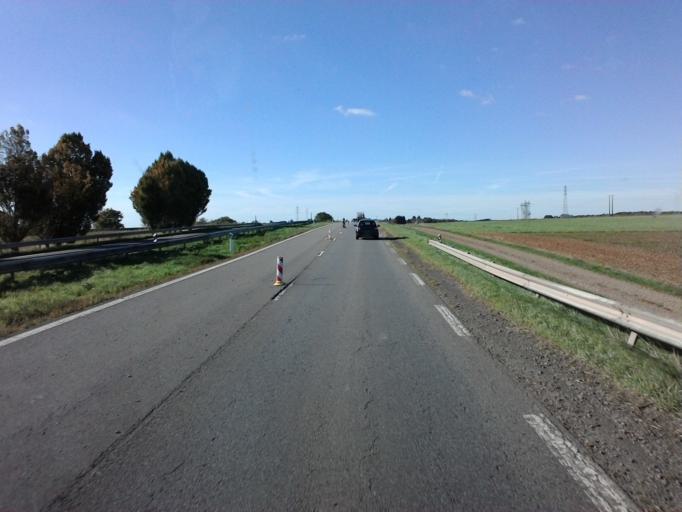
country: FR
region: Lorraine
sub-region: Departement de Meurthe-et-Moselle
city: Villers-la-Montagne
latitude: 49.4793
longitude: 5.8220
